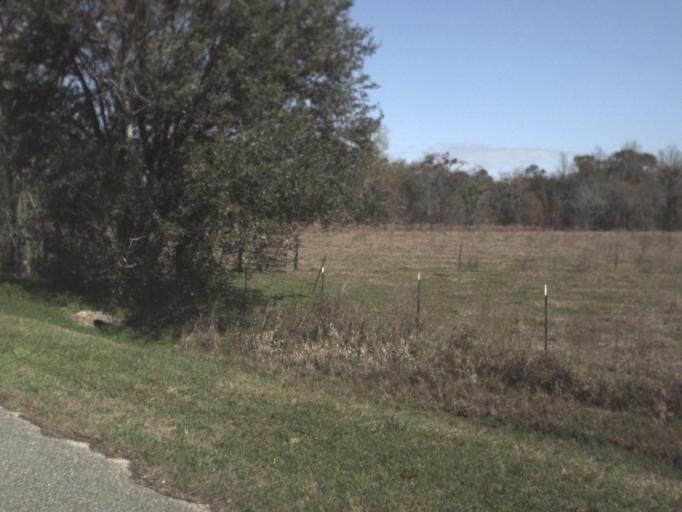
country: US
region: Florida
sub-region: Calhoun County
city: Blountstown
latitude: 30.5798
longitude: -85.0219
